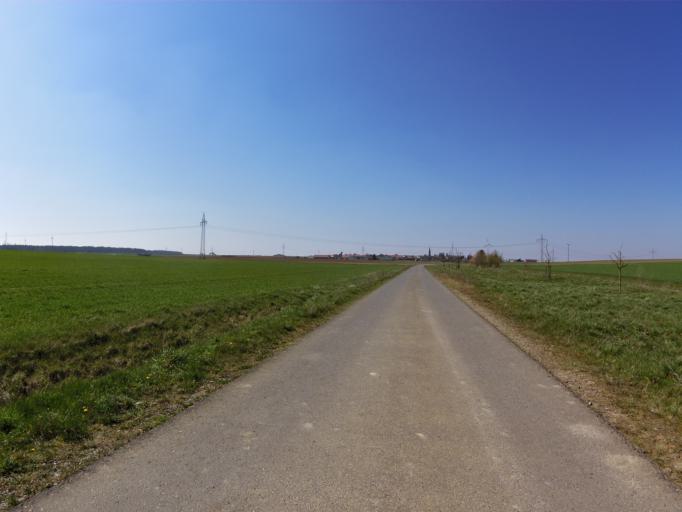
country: DE
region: Bavaria
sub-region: Regierungsbezirk Unterfranken
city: Biebelried
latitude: 49.7445
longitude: 10.0831
